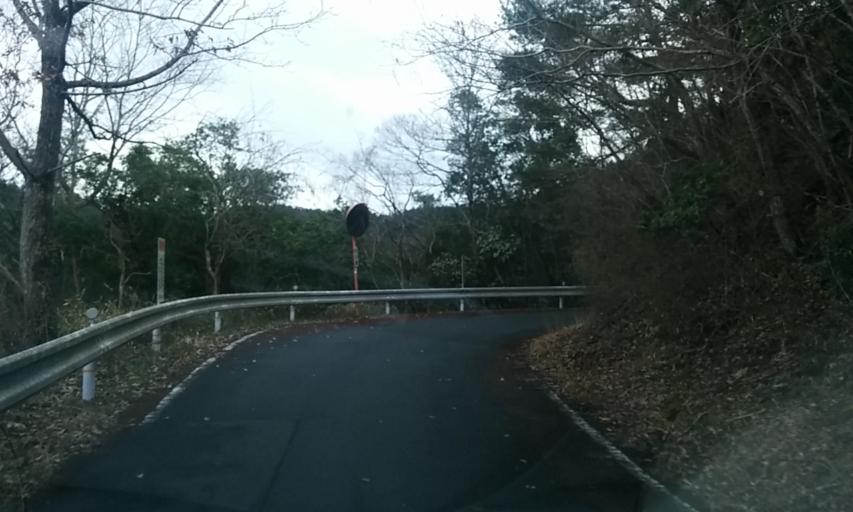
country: JP
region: Kyoto
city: Kameoka
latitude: 35.1134
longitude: 135.4302
